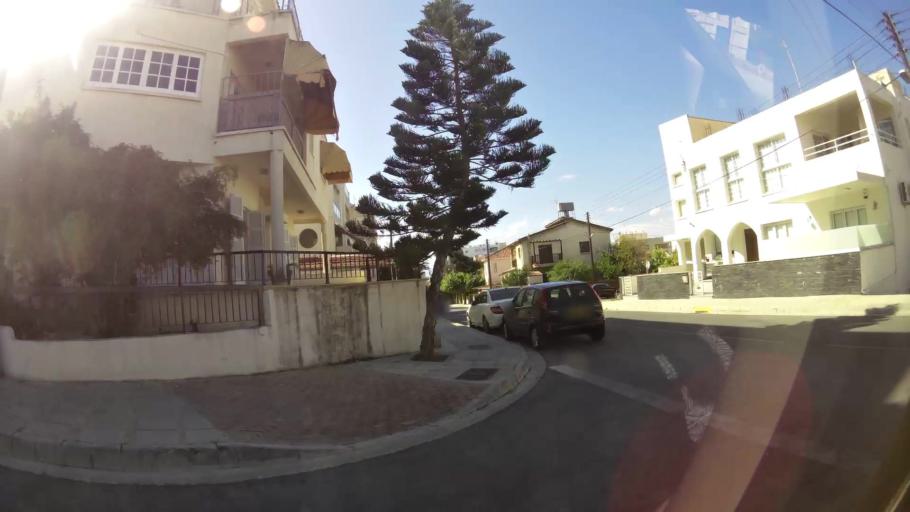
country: CY
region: Lefkosia
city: Nicosia
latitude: 35.1412
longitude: 33.3469
